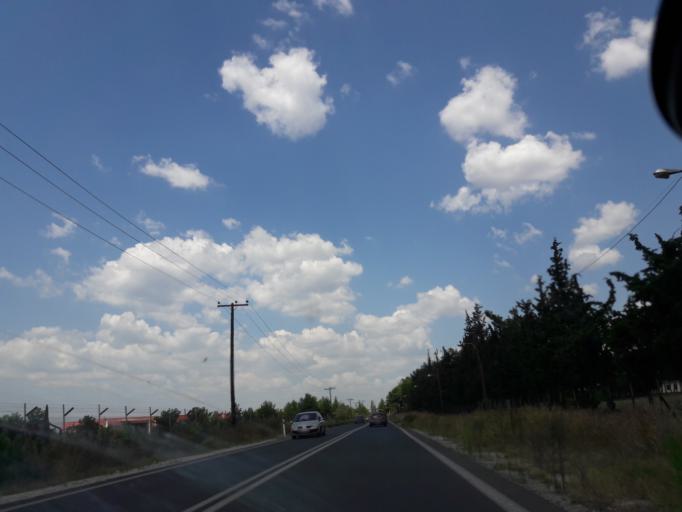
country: GR
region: Central Macedonia
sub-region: Nomos Thessalonikis
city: Thermi
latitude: 40.5354
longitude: 23.0369
